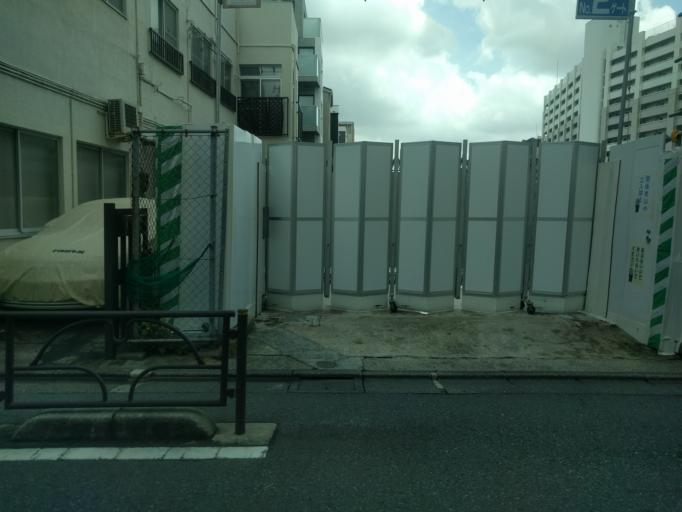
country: JP
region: Tokyo
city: Tokyo
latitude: 35.6043
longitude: 139.6718
